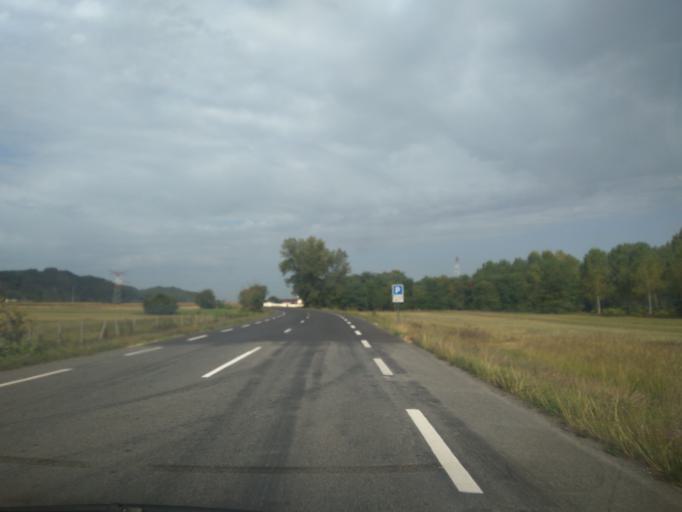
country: FR
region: Aquitaine
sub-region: Departement des Pyrenees-Atlantiques
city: Arbus
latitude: 43.3359
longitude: -0.4966
